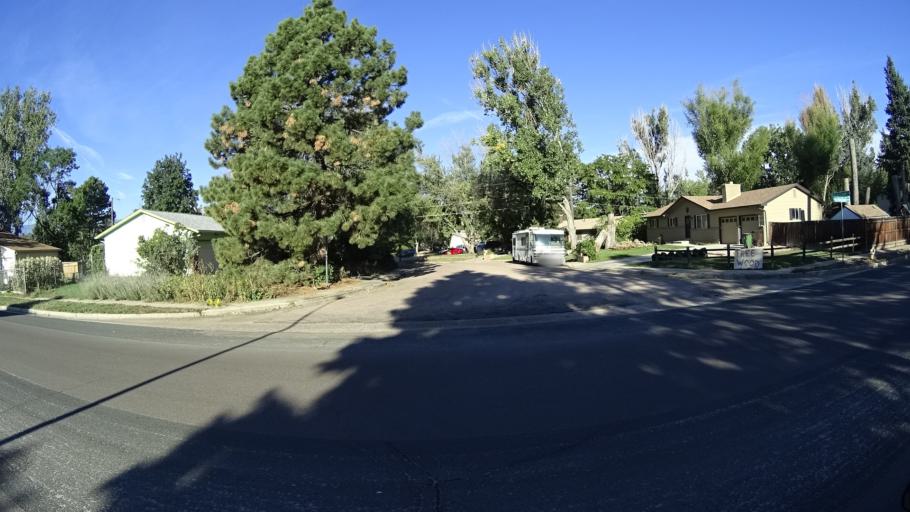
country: US
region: Colorado
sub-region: El Paso County
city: Cimarron Hills
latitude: 38.8929
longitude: -104.7663
